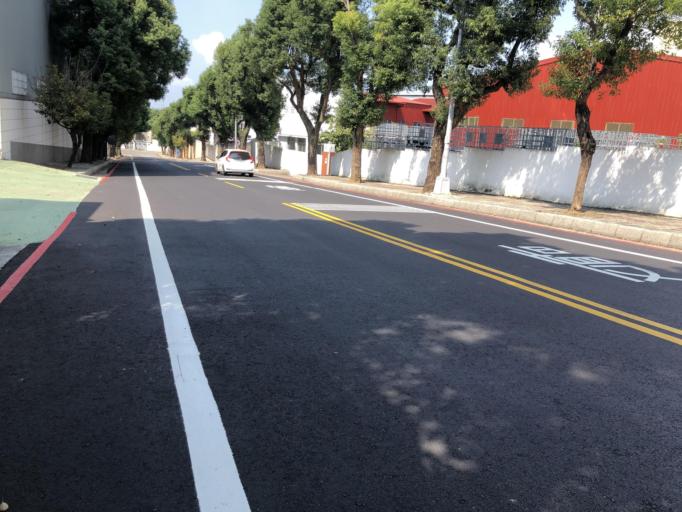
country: TW
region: Taiwan
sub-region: Miaoli
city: Miaoli
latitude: 24.4796
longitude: 120.7926
